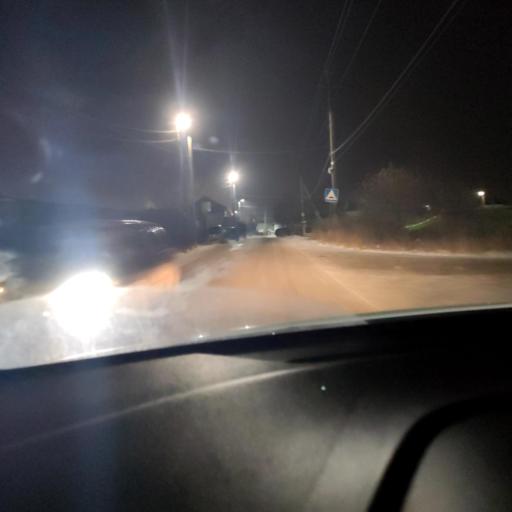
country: RU
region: Tatarstan
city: Staroye Arakchino
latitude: 55.8808
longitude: 49.0409
